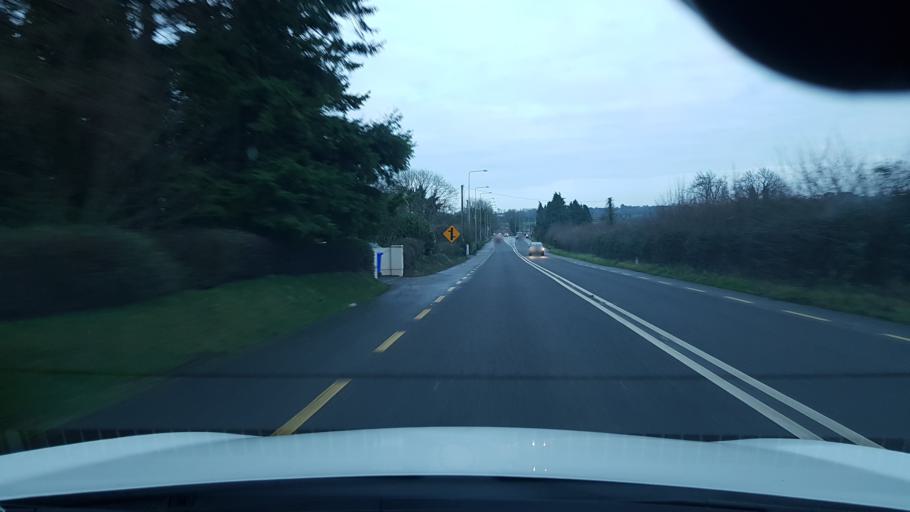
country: IE
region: Leinster
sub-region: An Mhi
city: Navan
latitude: 53.6060
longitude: -6.6235
